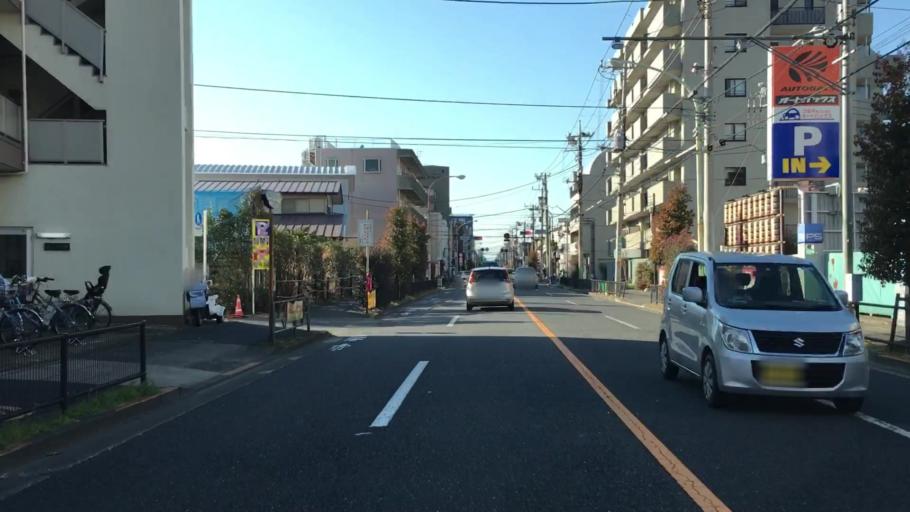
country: JP
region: Tokyo
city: Mitaka-shi
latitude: 35.6909
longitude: 139.6103
